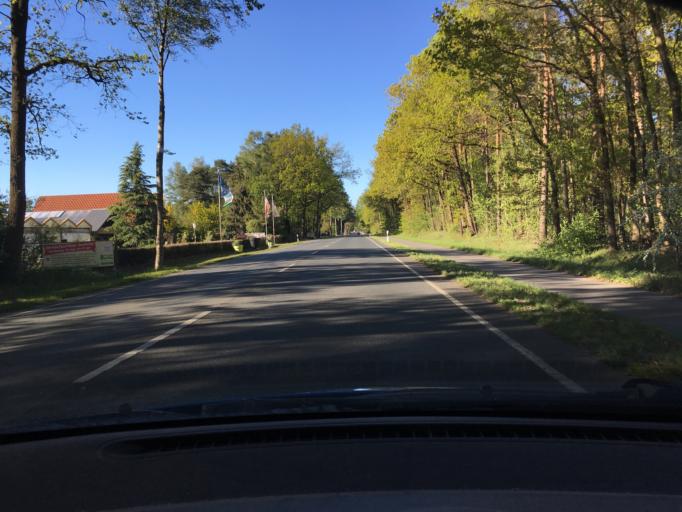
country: DE
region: Lower Saxony
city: Soltau
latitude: 53.0646
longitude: 9.8596
